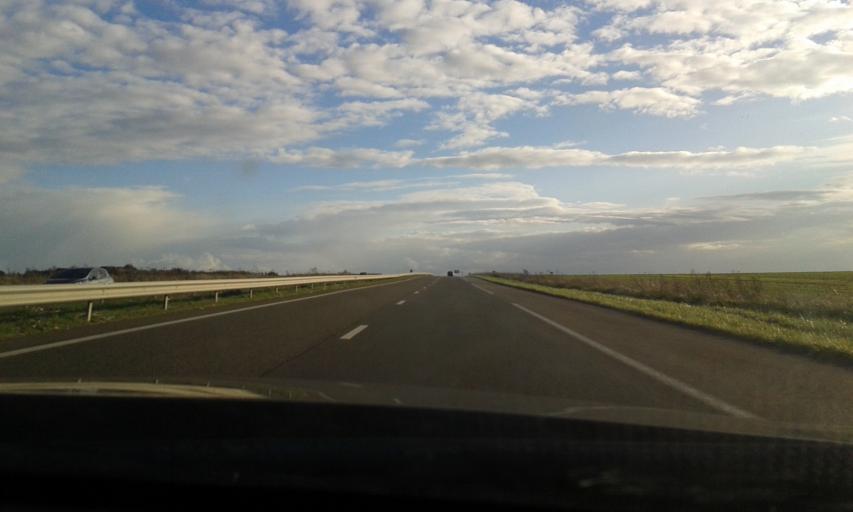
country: FR
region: Centre
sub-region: Departement d'Eure-et-Loir
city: Bailleau-l'Eveque
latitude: 48.5483
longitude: 1.4483
